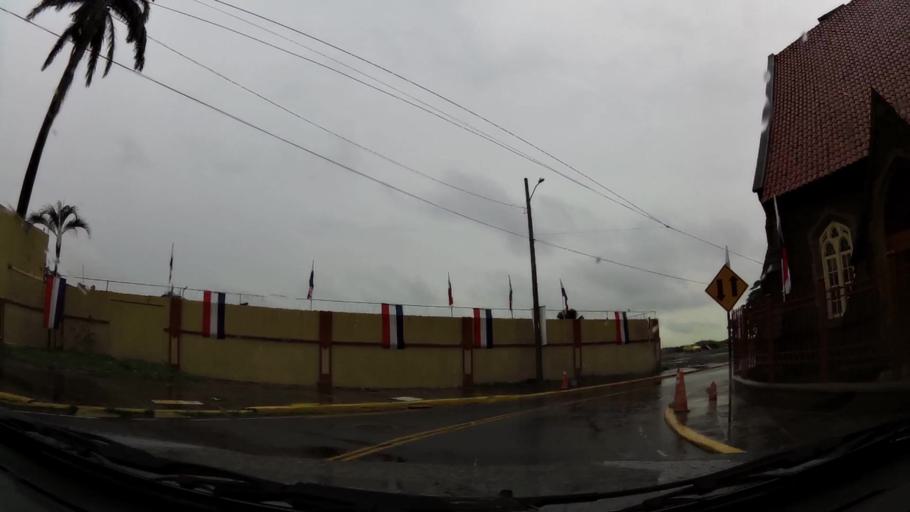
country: PA
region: Colon
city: Colon
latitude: 9.3651
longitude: -79.9062
